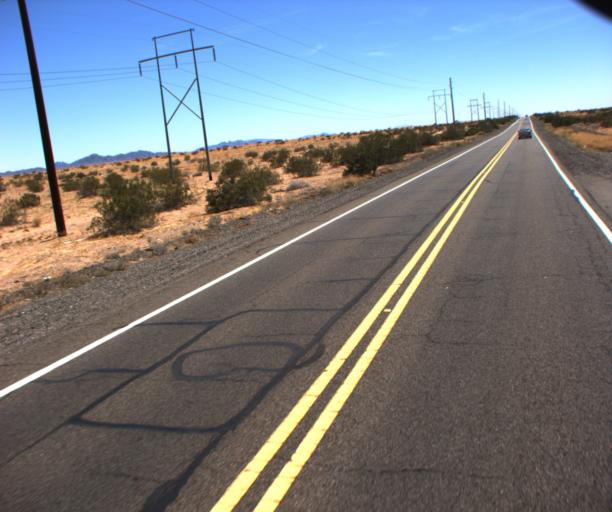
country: US
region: Arizona
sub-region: La Paz County
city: Parker
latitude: 33.9531
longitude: -114.2169
